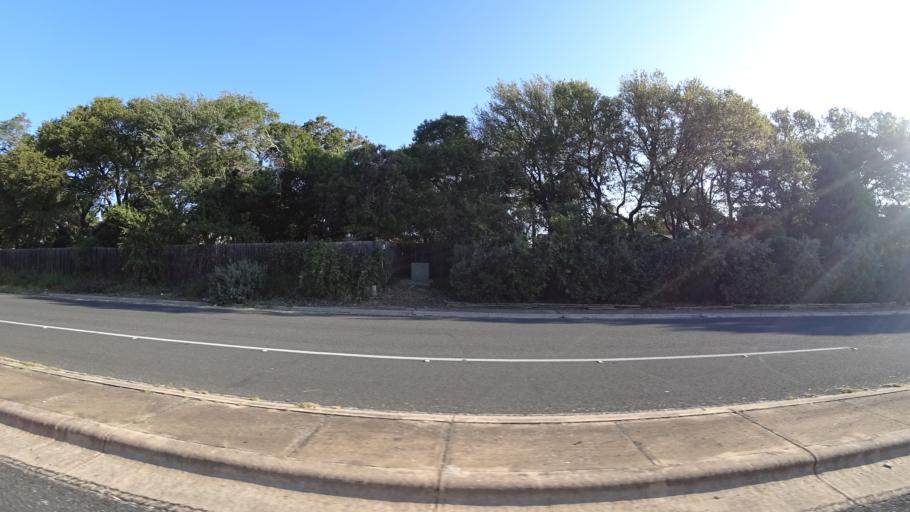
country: US
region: Texas
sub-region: Travis County
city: Rollingwood
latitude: 30.2610
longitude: -97.8071
